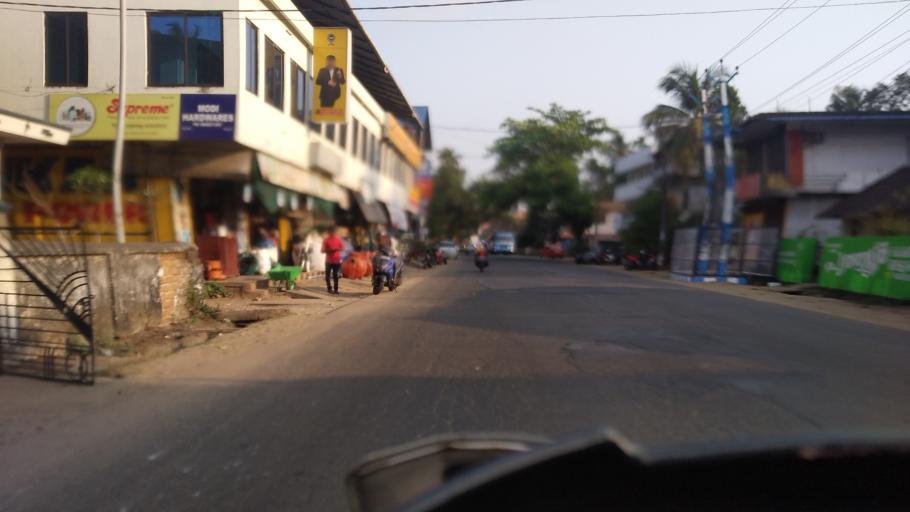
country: IN
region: Kerala
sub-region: Thrissur District
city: Thanniyam
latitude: 10.4015
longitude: 76.1128
